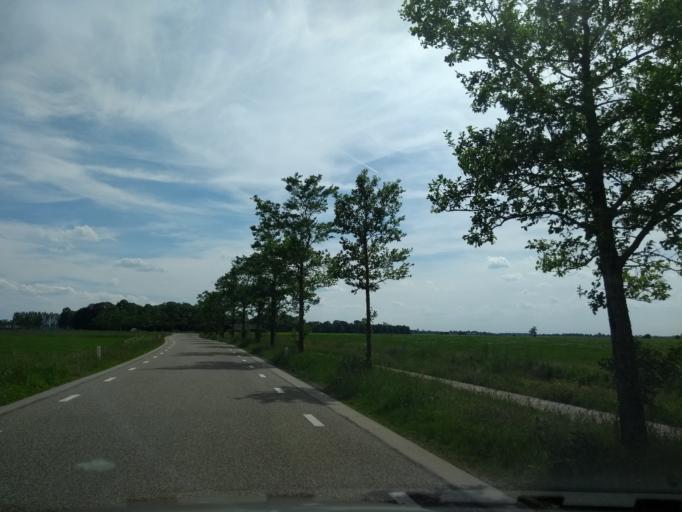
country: NL
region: Groningen
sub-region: Gemeente Zuidhorn
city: Oldehove
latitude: 53.2829
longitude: 6.4235
